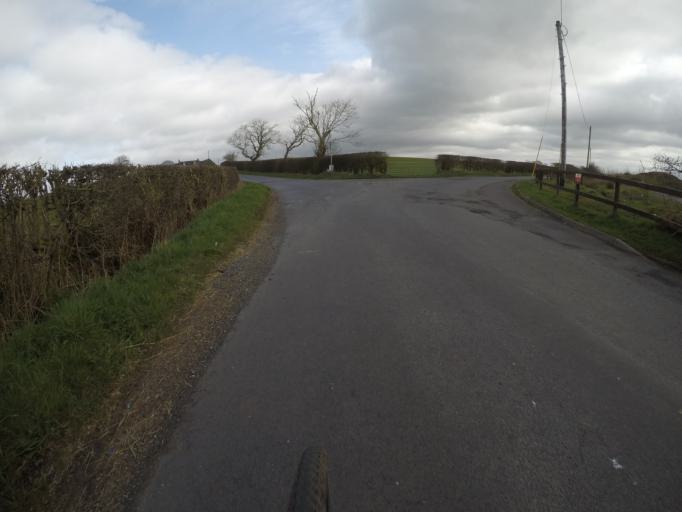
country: GB
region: Scotland
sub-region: North Ayrshire
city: Springside
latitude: 55.6603
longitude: -4.6081
